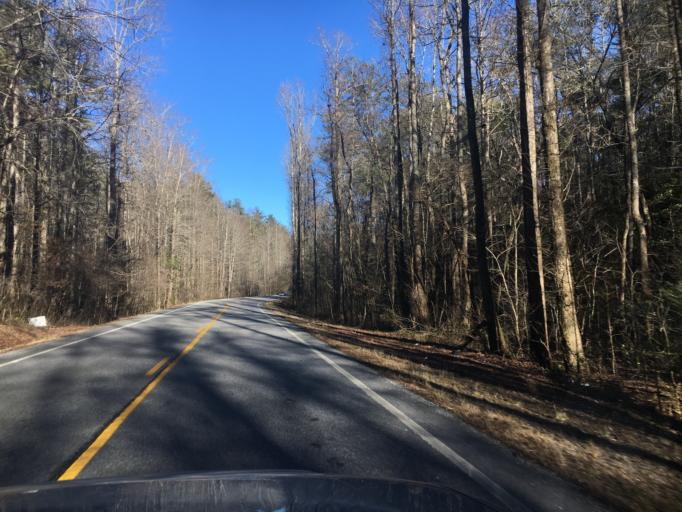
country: US
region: Georgia
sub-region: White County
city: Cleveland
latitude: 34.6630
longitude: -83.8889
